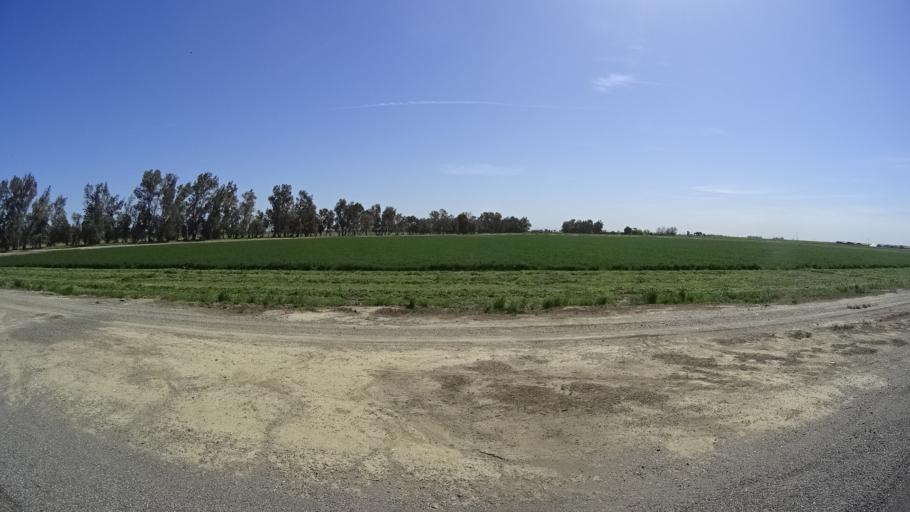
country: US
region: California
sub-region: Glenn County
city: Hamilton City
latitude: 39.6853
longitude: -122.1033
